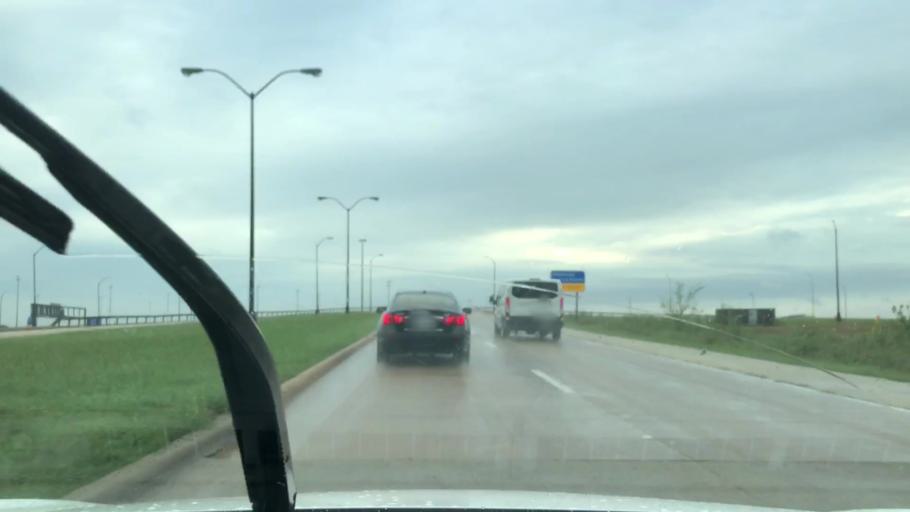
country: US
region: Texas
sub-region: Dallas County
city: Coppell
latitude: 32.9263
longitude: -97.0373
